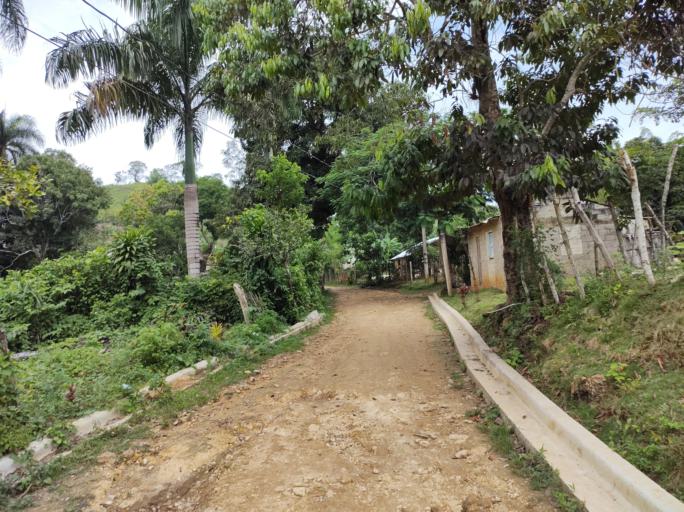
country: DO
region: Samana
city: Las Terrenas
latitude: 19.2827
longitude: -69.4378
